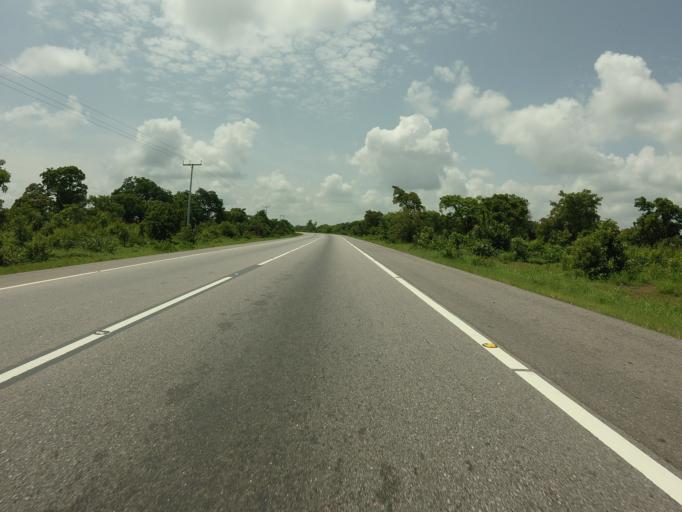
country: GH
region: Northern
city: Tamale
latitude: 9.1282
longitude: -1.2237
